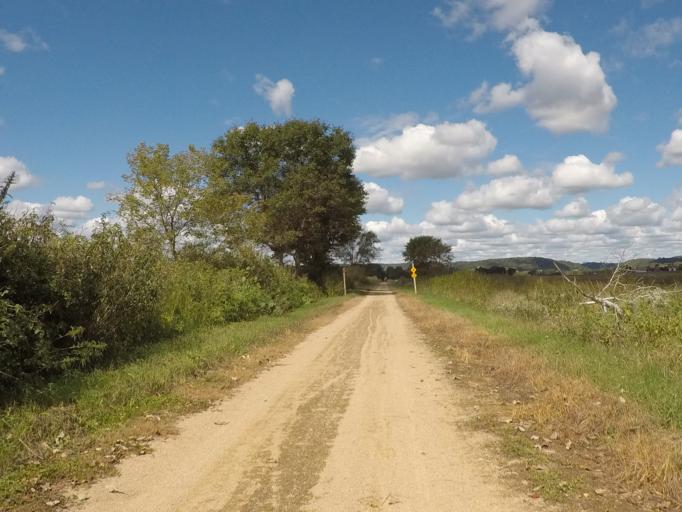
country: US
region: Wisconsin
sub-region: Richland County
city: Richland Center
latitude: 43.2955
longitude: -90.3304
